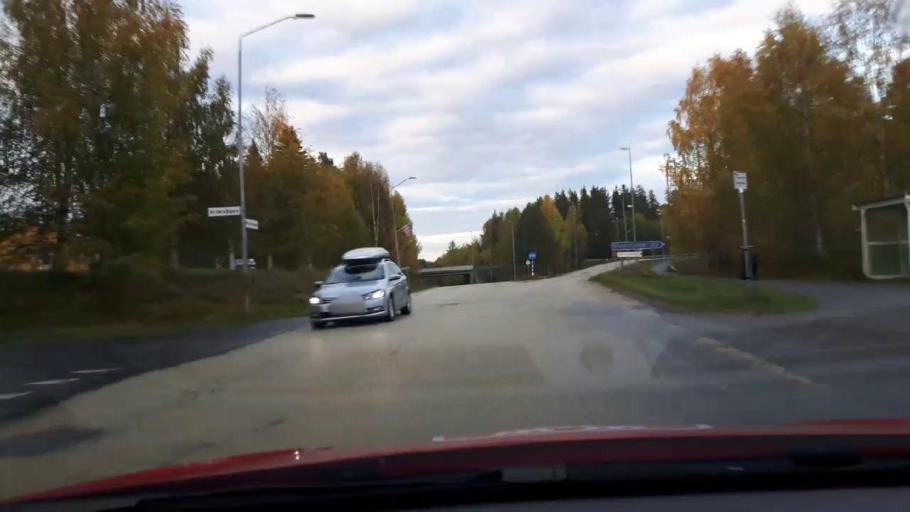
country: SE
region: Jaemtland
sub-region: OEstersunds Kommun
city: Lit
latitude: 63.3200
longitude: 14.8587
